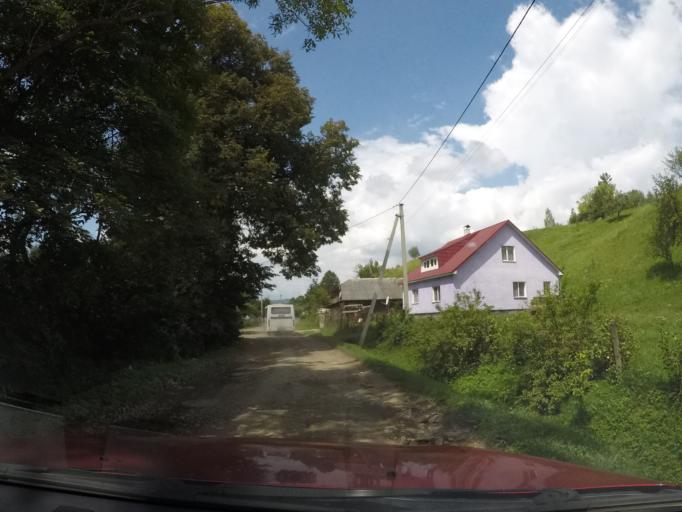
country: UA
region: Zakarpattia
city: Velykyi Bereznyi
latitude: 49.0238
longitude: 22.6092
